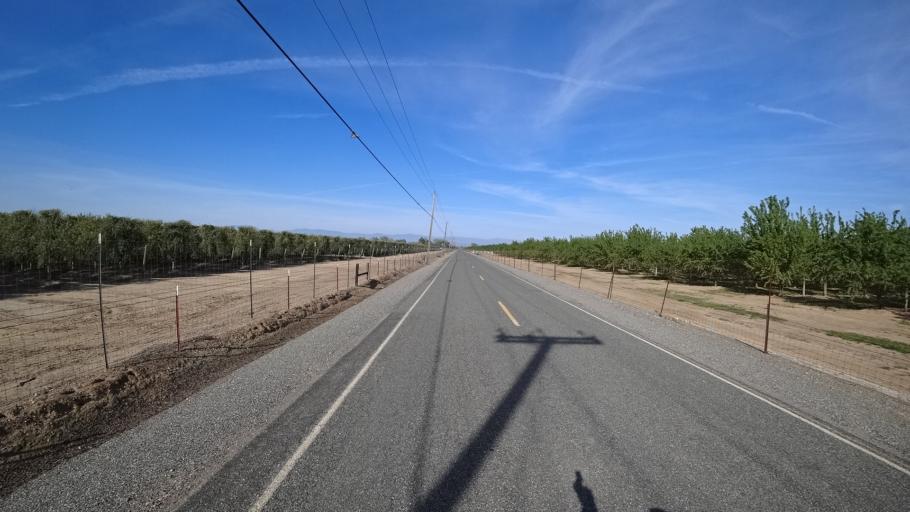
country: US
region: California
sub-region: Glenn County
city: Orland
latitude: 39.6679
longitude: -122.2081
